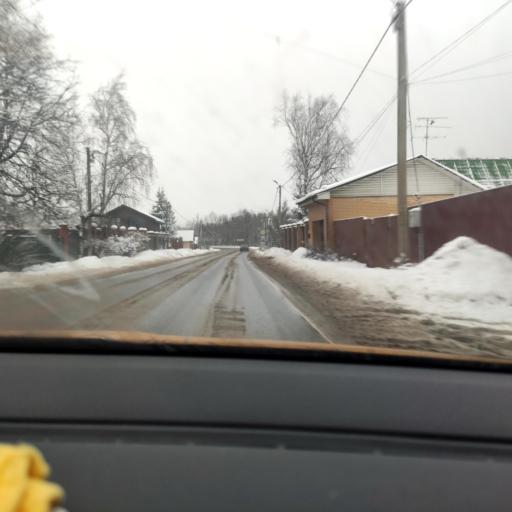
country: RU
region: Moskovskaya
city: Zvenigorod
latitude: 55.7510
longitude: 36.8752
